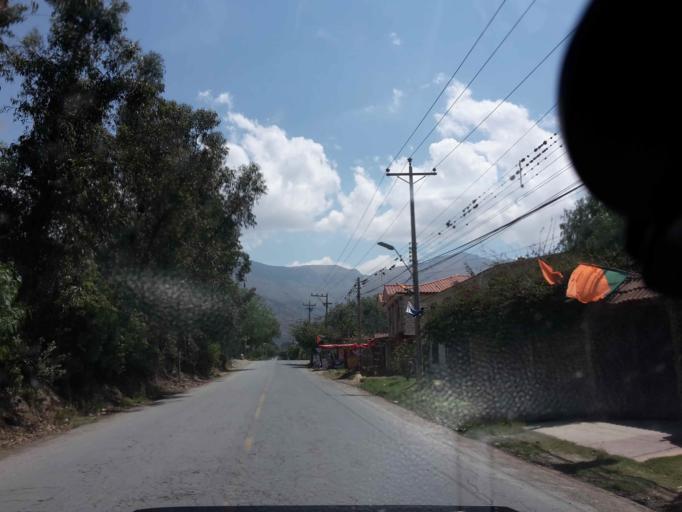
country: BO
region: Cochabamba
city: Cochabamba
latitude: -17.3563
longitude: -66.2274
